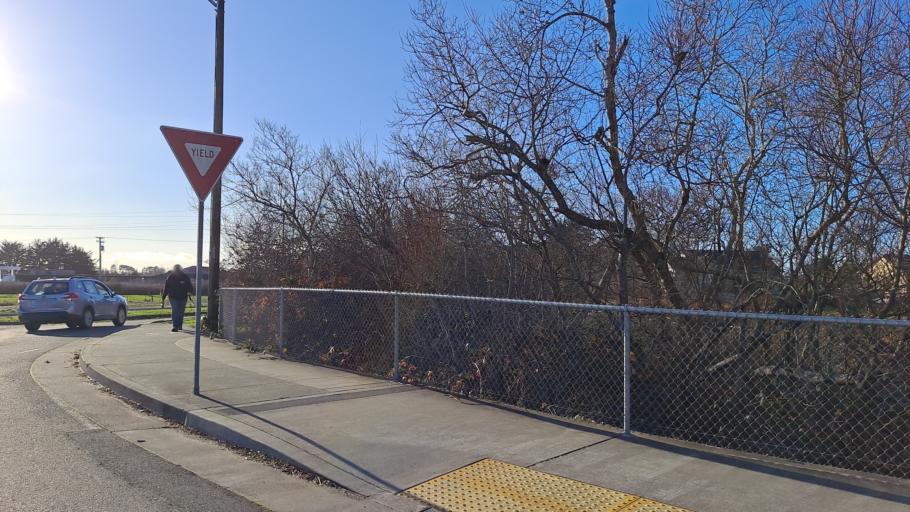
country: US
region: California
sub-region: Humboldt County
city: Arcata
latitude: 40.8618
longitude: -124.0772
